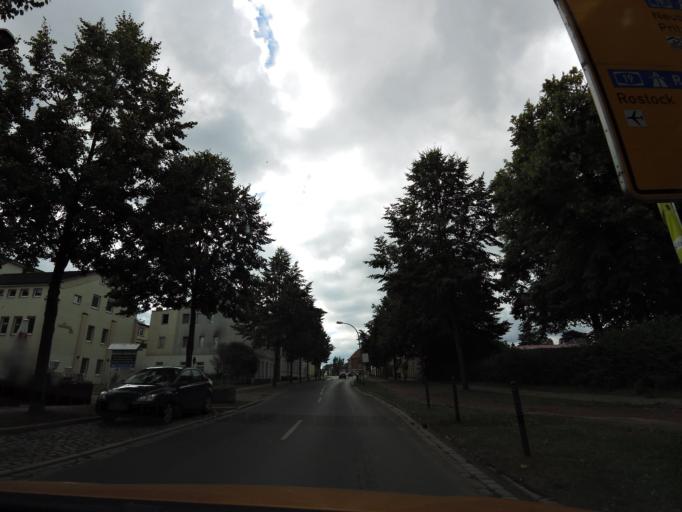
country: DE
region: Mecklenburg-Vorpommern
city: Guestrow
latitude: 53.7895
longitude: 12.1805
